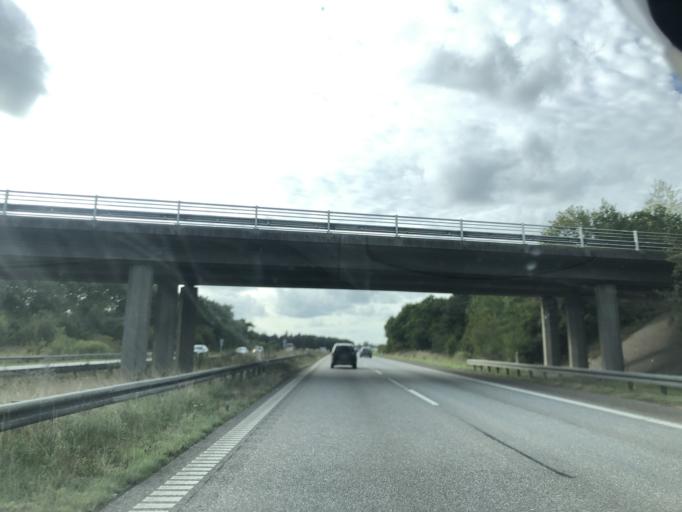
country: DK
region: Zealand
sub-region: Koge Kommune
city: Borup
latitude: 55.4570
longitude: 11.9836
